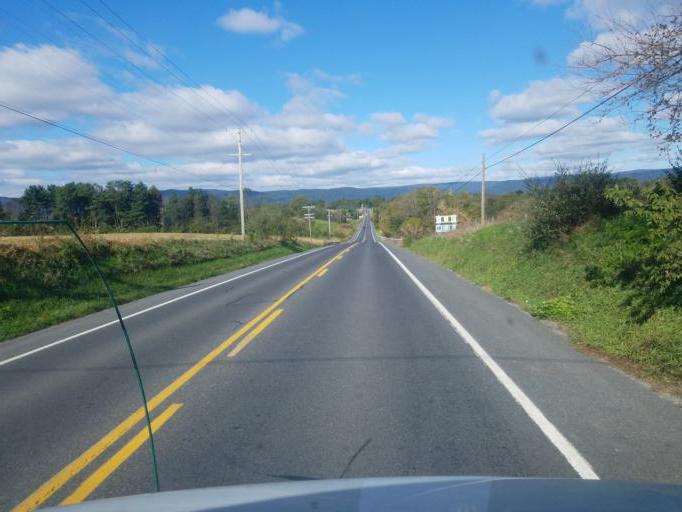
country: US
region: Pennsylvania
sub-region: Franklin County
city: Mercersburg
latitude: 39.8135
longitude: -77.8865
